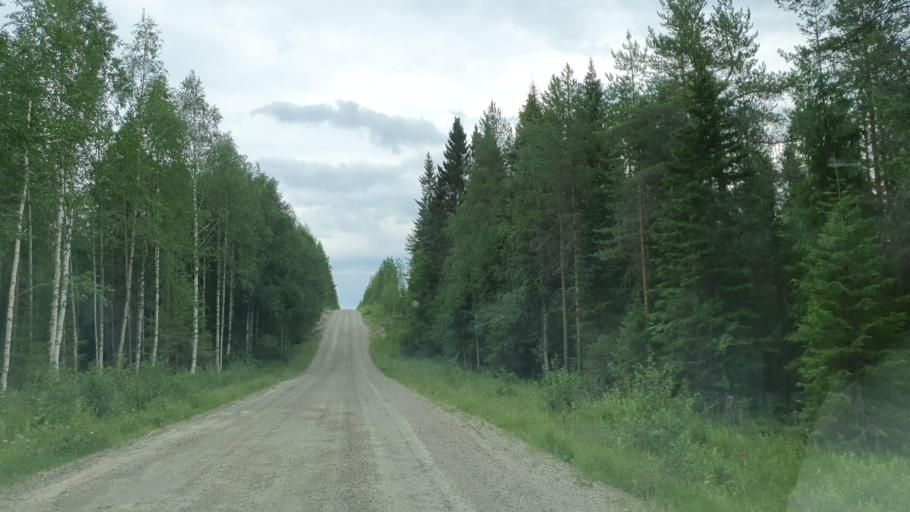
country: FI
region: Kainuu
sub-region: Kehys-Kainuu
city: Kuhmo
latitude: 64.7533
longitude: 29.8664
